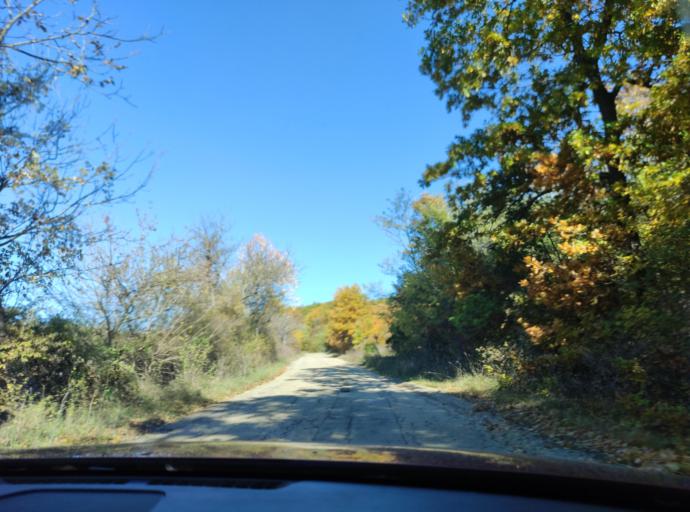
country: BG
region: Montana
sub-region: Obshtina Montana
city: Montana
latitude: 43.4048
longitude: 23.0827
